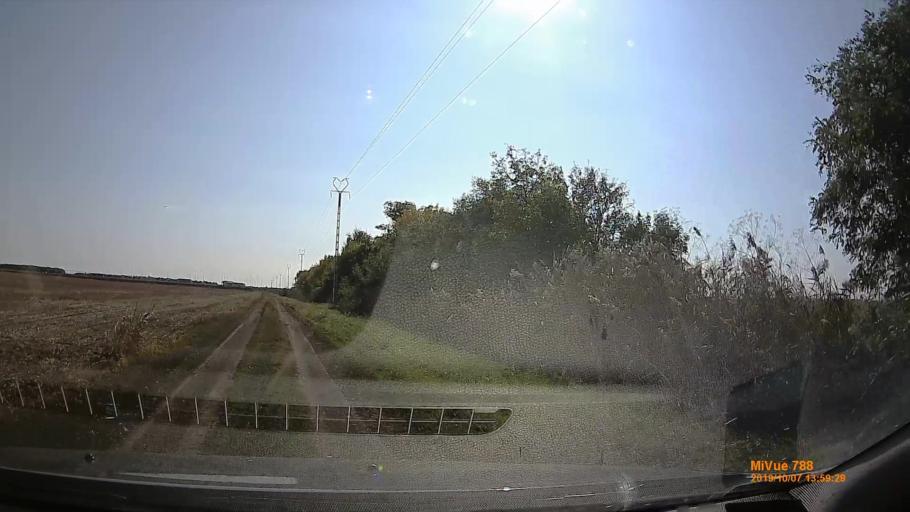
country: HU
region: Jasz-Nagykun-Szolnok
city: Cserkeszolo
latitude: 46.8897
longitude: 20.2143
